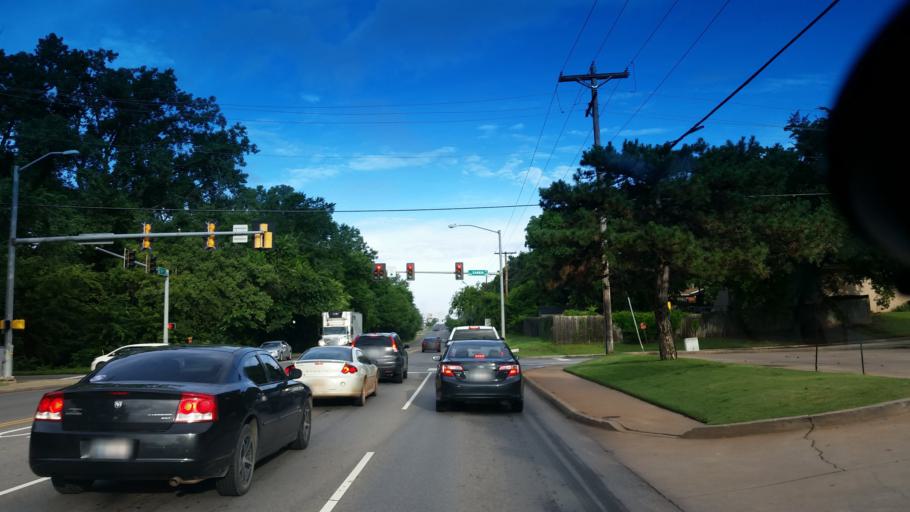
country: US
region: Oklahoma
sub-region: Oklahoma County
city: Edmond
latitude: 35.6384
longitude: -97.4733
